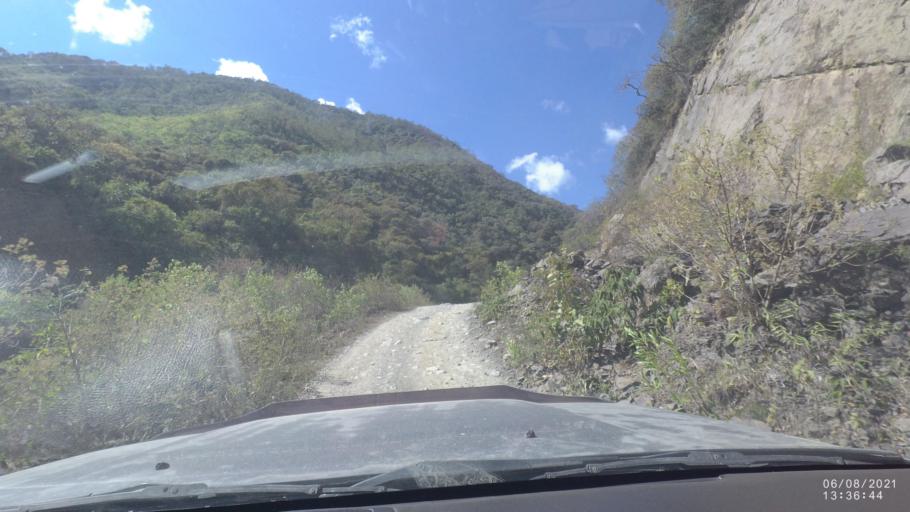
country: BO
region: La Paz
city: Quime
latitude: -16.6902
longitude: -66.7220
